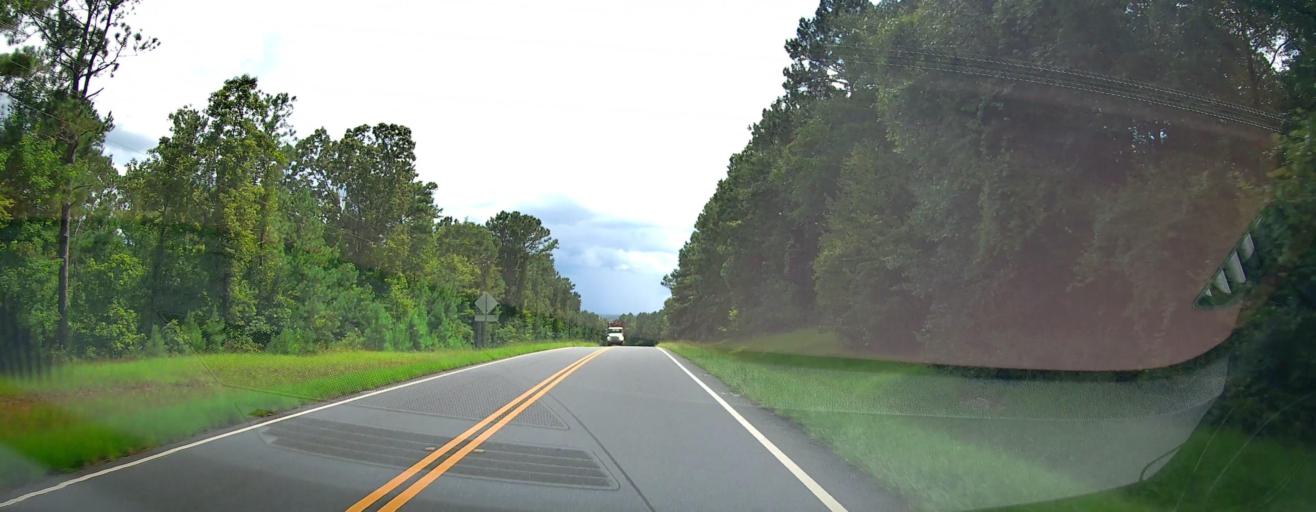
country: US
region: Georgia
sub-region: Monroe County
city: Forsyth
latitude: 32.8820
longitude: -83.9731
